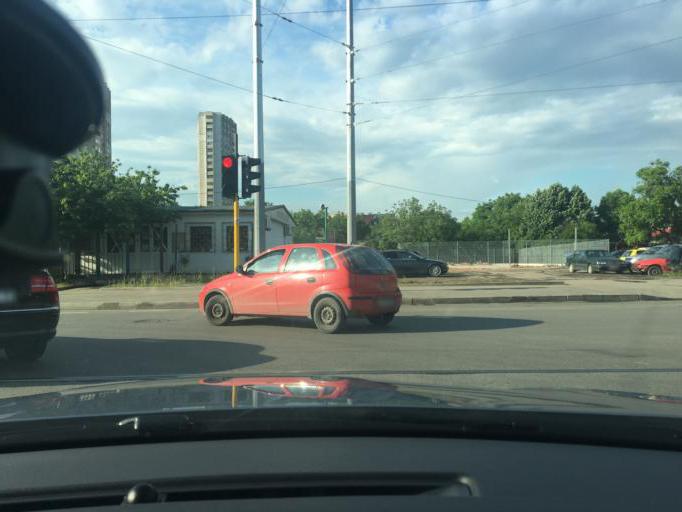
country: BG
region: Sofia-Capital
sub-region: Stolichna Obshtina
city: Sofia
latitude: 42.6750
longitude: 23.3761
